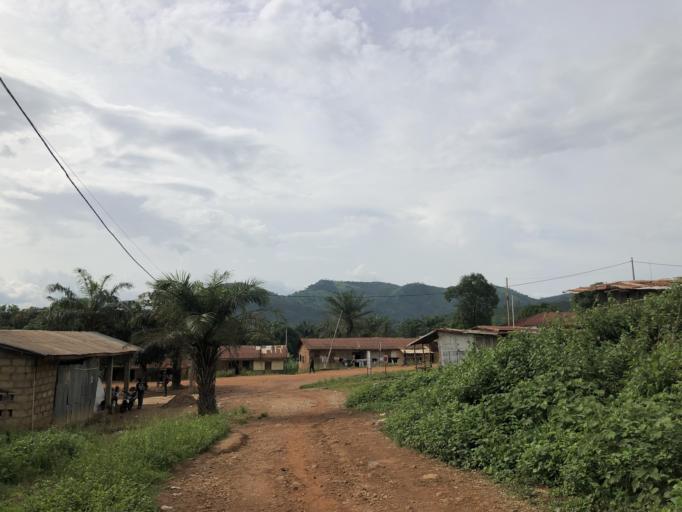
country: SL
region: Northern Province
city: Bumbuna
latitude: 9.0429
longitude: -11.7422
